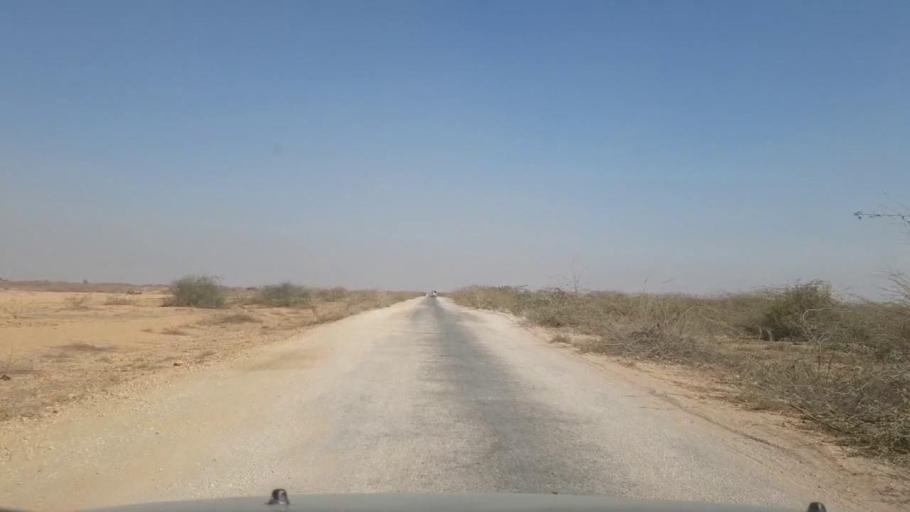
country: PK
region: Sindh
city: Thatta
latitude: 24.8930
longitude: 67.9154
